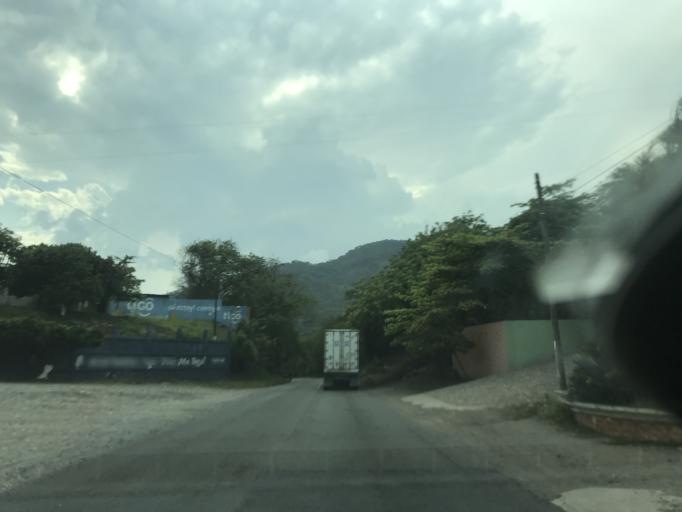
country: GT
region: Zacapa
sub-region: Municipio de Zacapa
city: Gualan
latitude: 15.2073
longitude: -89.2466
